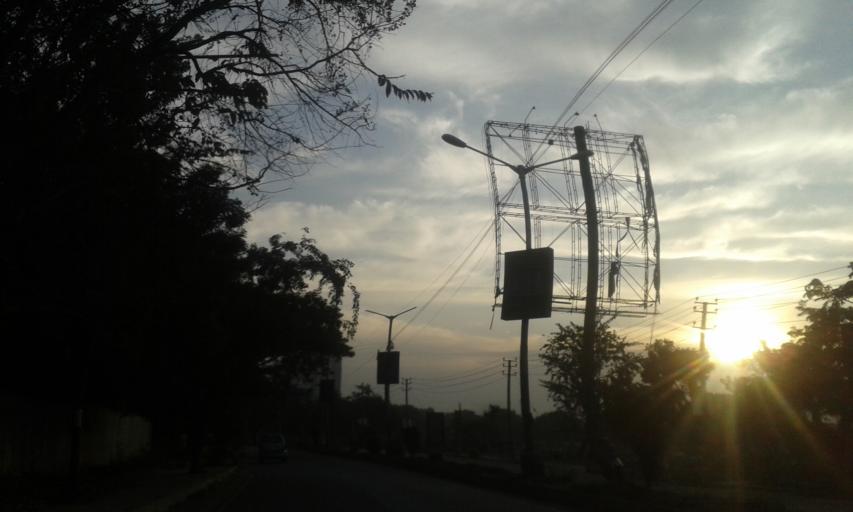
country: IN
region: Karnataka
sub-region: Bangalore Rural
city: Hoskote
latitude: 12.9904
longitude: 77.7554
